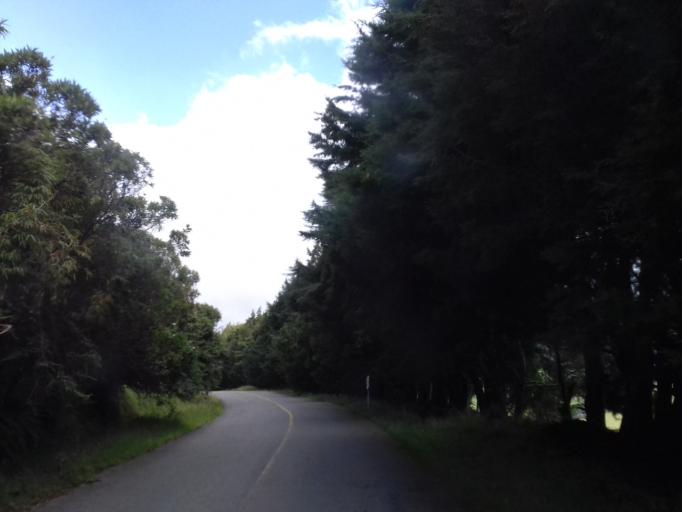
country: CO
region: Caldas
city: Villamaria
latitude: 5.0154
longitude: -75.3385
